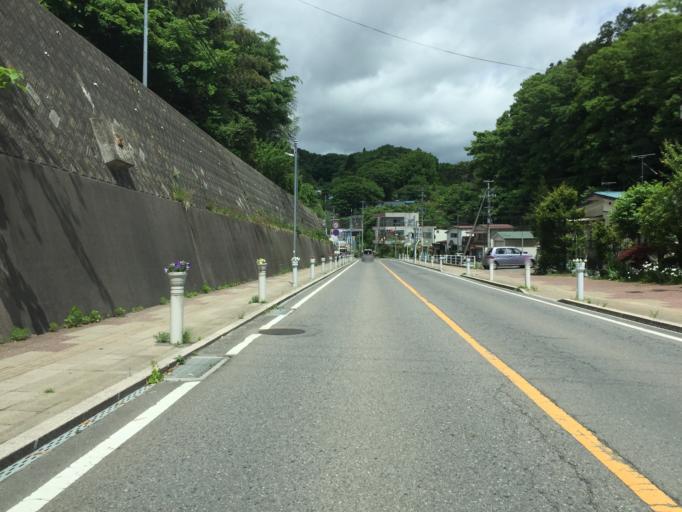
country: JP
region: Fukushima
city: Miharu
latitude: 37.4463
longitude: 140.4876
